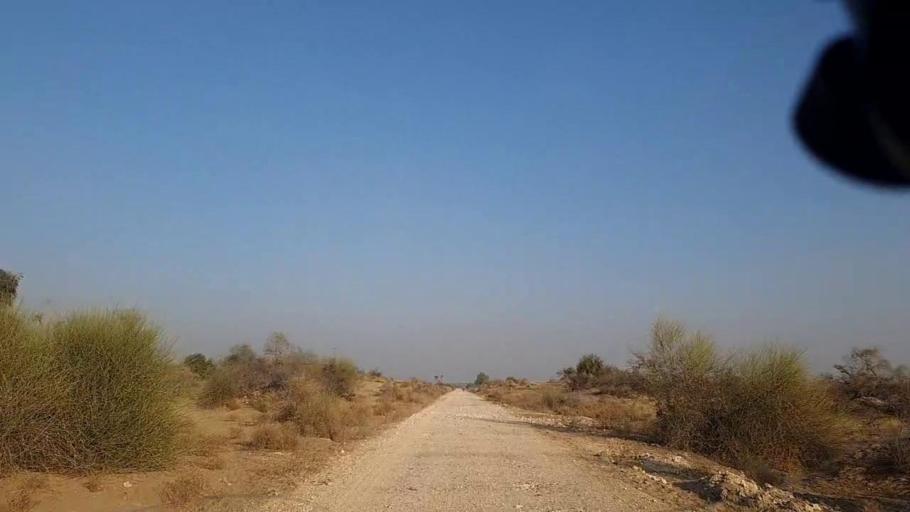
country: PK
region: Sindh
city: Khanpur
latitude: 27.6138
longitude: 69.5361
